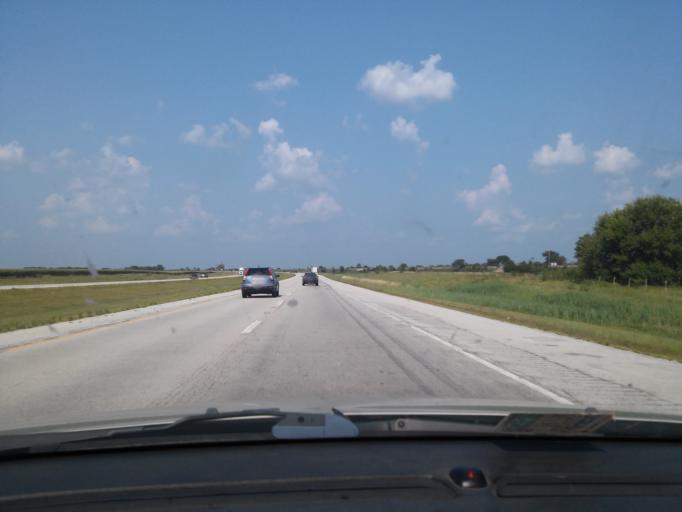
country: US
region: Illinois
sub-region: Livingston County
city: Pontiac
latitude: 40.9461
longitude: -88.5832
